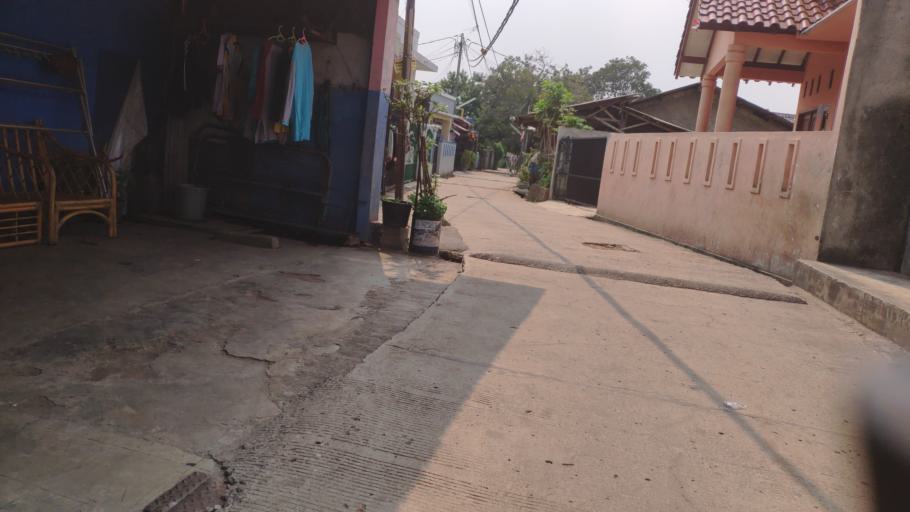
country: ID
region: West Java
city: Depok
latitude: -6.3865
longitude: 106.8040
